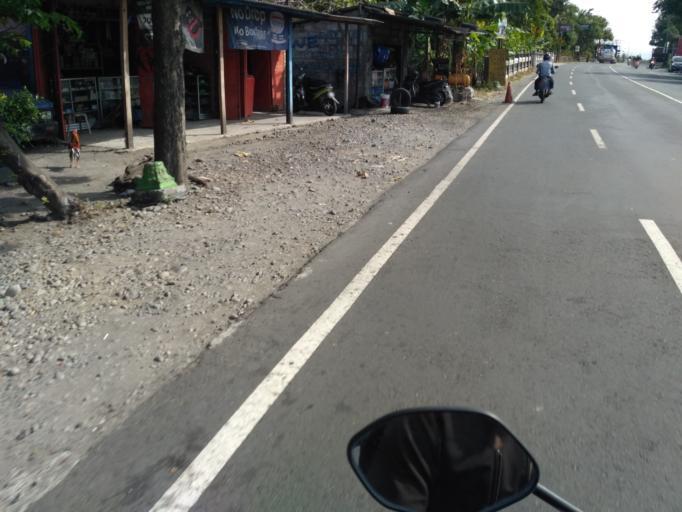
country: ID
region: Daerah Istimewa Yogyakarta
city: Godean
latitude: -7.8112
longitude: 110.2786
